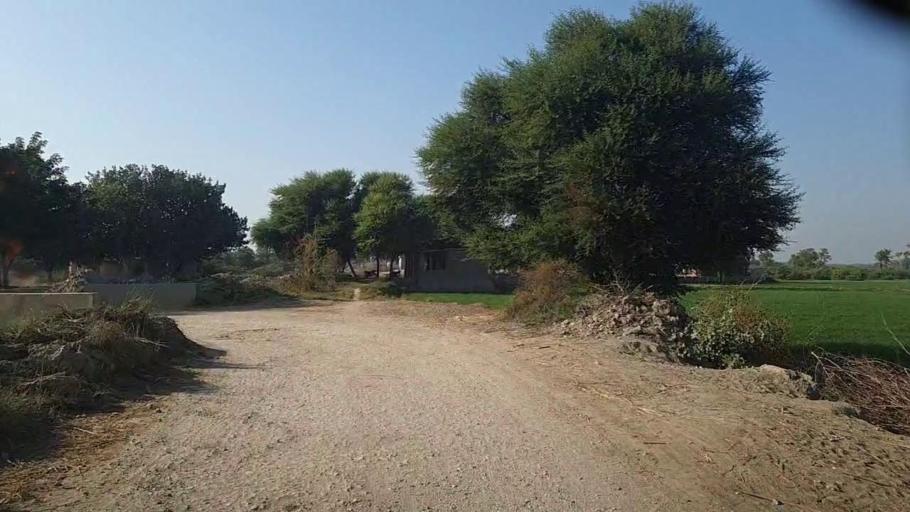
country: PK
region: Sindh
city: Darya Khan Marri
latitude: 26.6789
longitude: 68.3713
